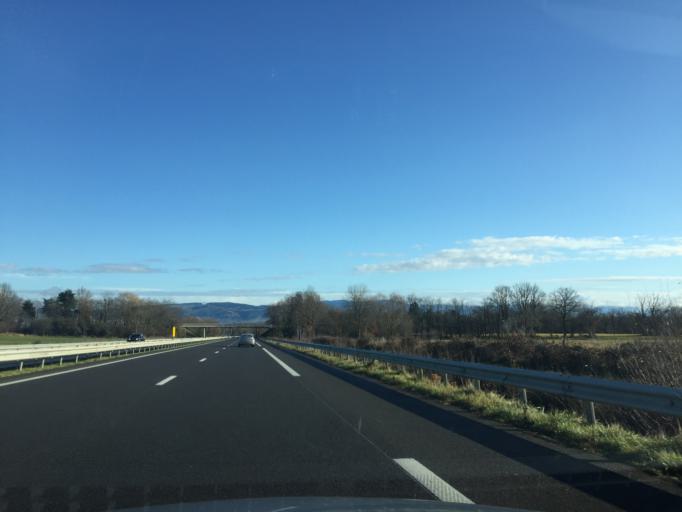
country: FR
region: Auvergne
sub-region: Departement du Puy-de-Dome
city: Orleat
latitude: 45.8502
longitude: 3.4215
